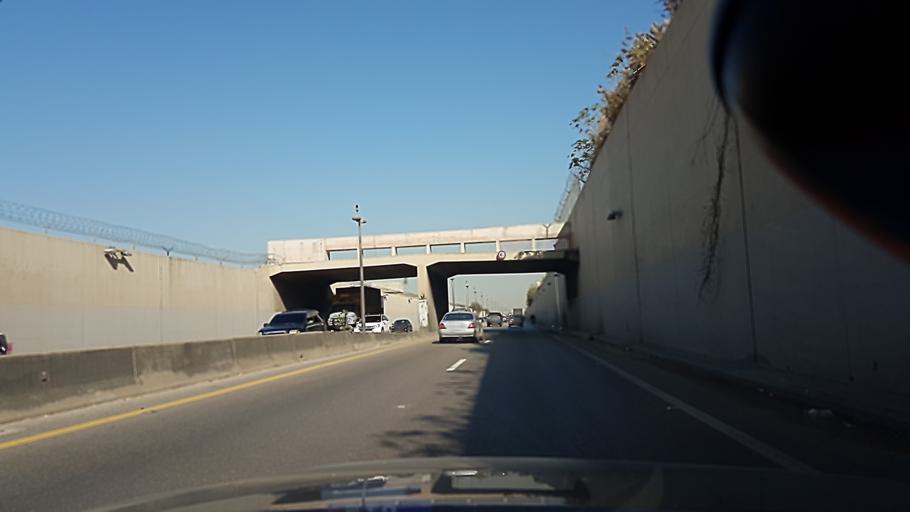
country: LB
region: Mont-Liban
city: Baabda
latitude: 33.8011
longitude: 35.4855
